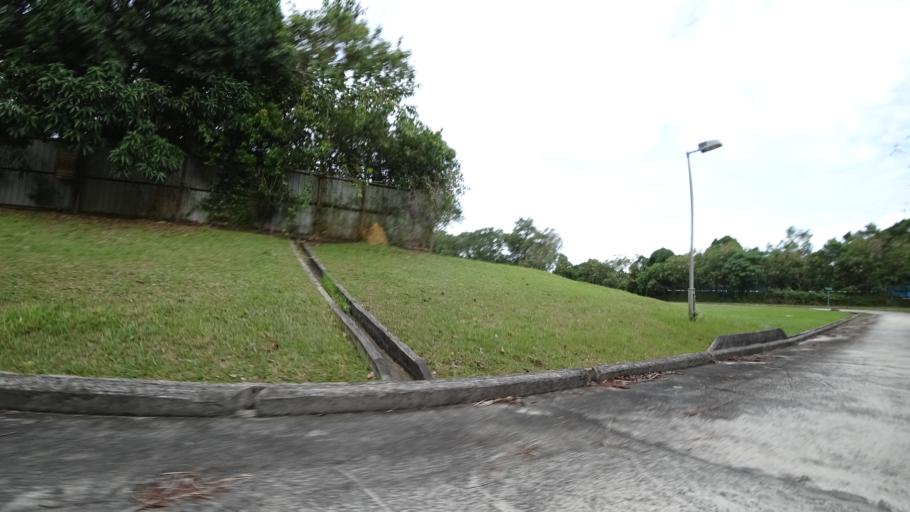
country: BN
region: Brunei and Muara
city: Bandar Seri Begawan
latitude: 4.9299
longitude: 114.9421
